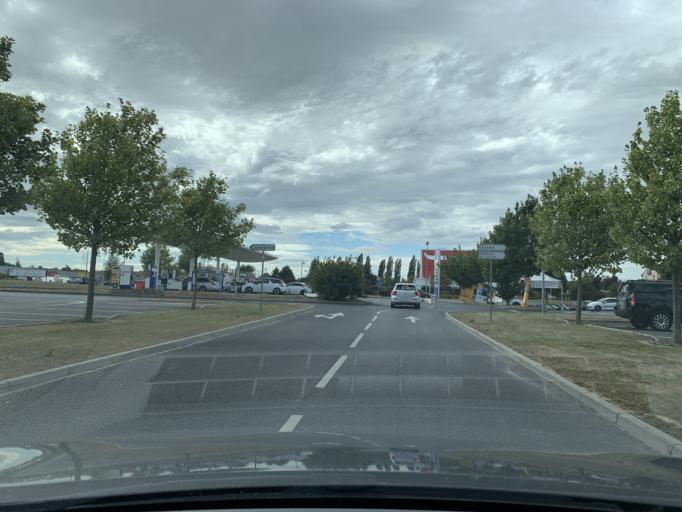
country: FR
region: Nord-Pas-de-Calais
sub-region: Departement du Nord
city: Caudry
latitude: 50.1290
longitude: 3.4269
